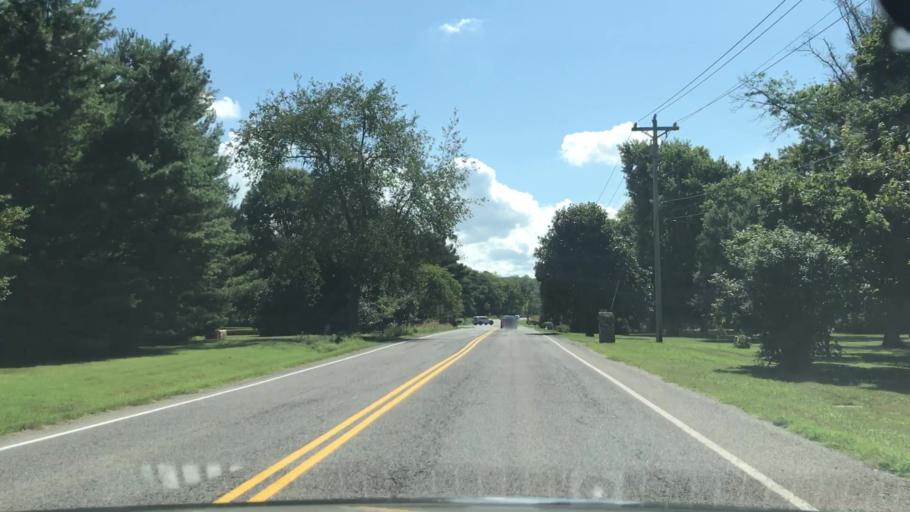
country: US
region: Tennessee
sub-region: Williamson County
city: Franklin
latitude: 35.9773
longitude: -86.8783
